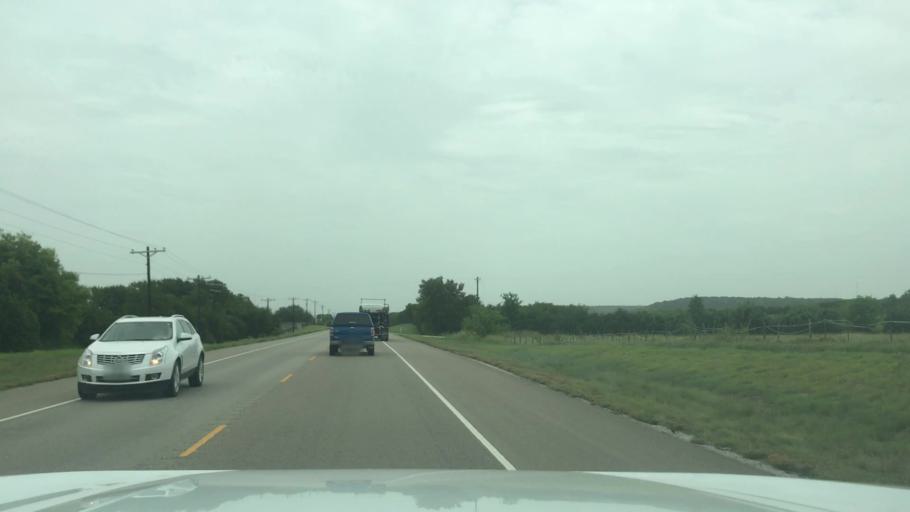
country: US
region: Texas
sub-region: Bosque County
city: Meridian
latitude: 31.9332
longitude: -97.6976
